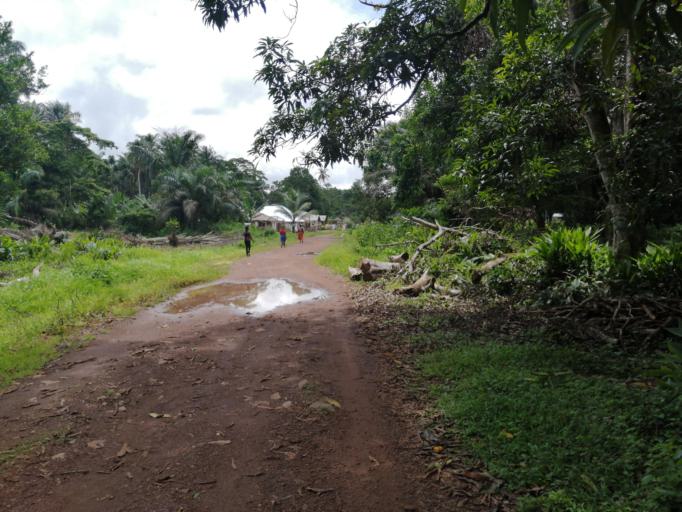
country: SL
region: Northern Province
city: Port Loko
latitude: 8.7895
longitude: -12.7731
